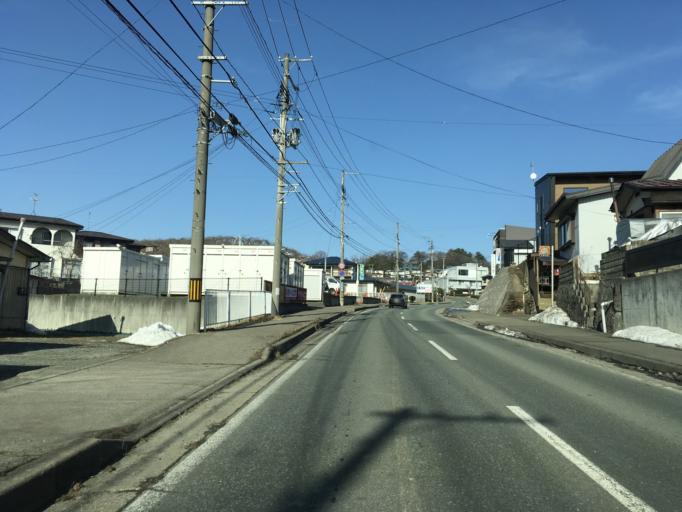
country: JP
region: Iwate
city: Morioka-shi
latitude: 39.7203
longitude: 141.1553
